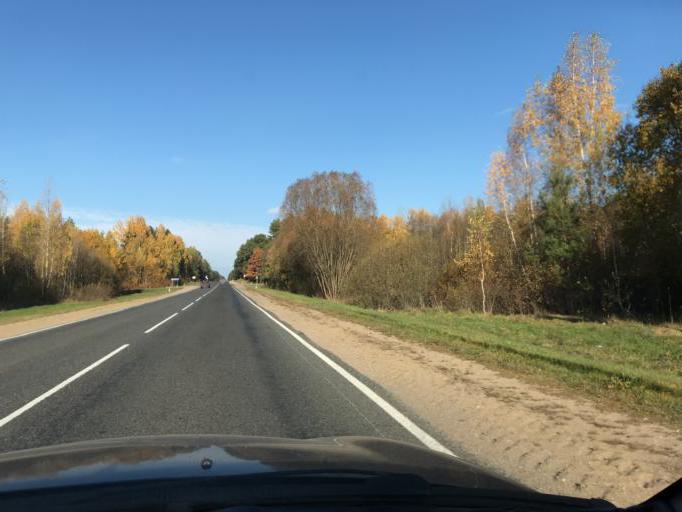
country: BY
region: Grodnenskaya
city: Lida
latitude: 53.9565
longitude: 25.2440
